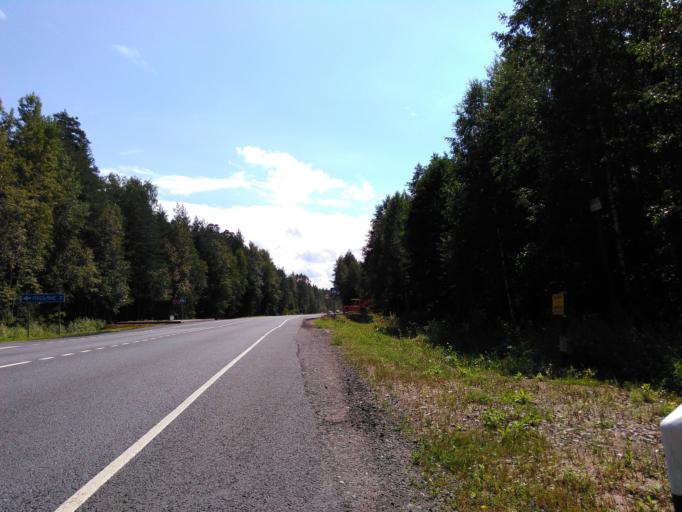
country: RU
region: Moskovskaya
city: Elektrogorsk
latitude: 56.0231
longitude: 38.7611
